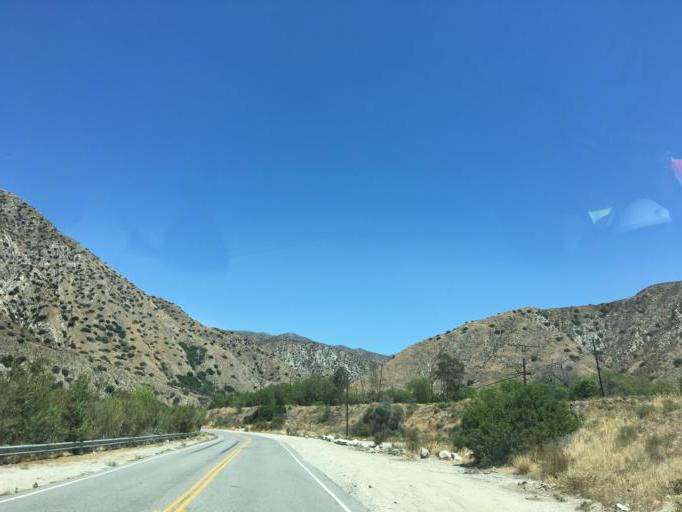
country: US
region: California
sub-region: Los Angeles County
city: La Crescenta-Montrose
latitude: 34.2839
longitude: -118.2921
